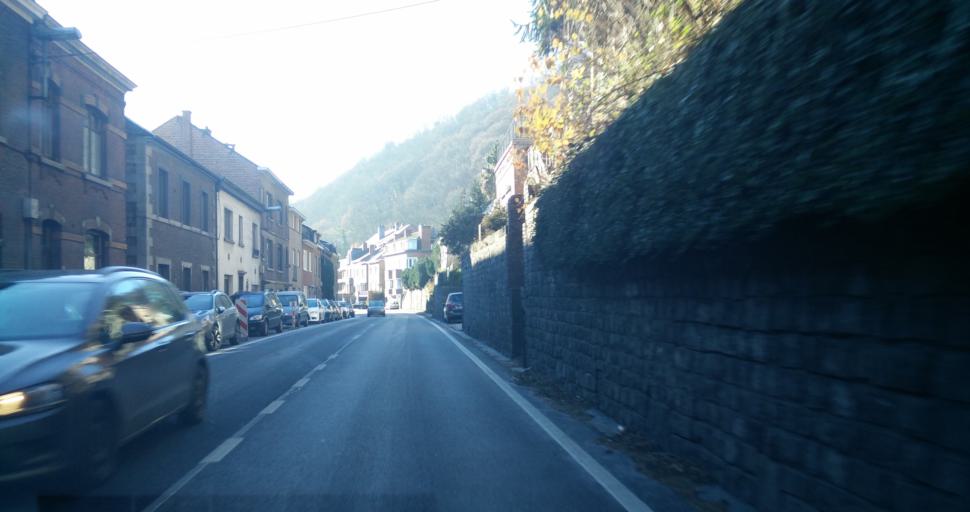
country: BE
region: Wallonia
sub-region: Province de Namur
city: Namur
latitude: 50.4515
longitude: 4.8575
